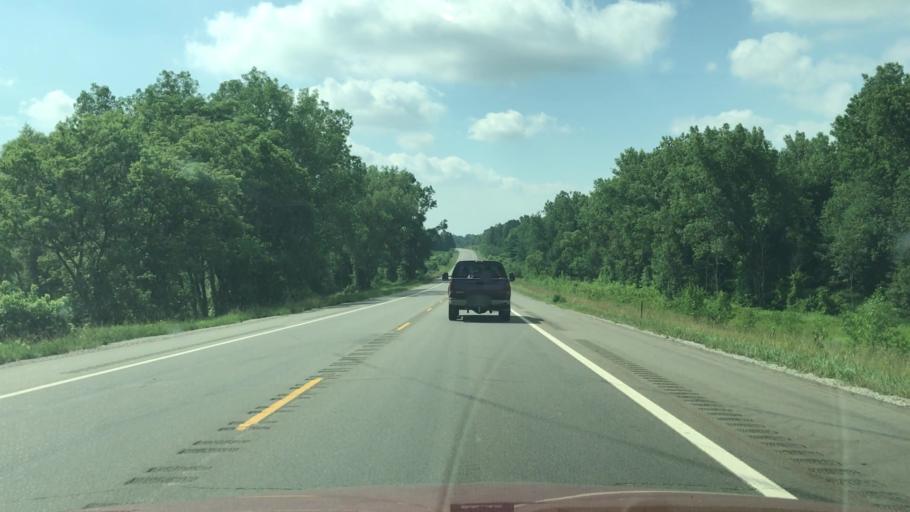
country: US
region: Michigan
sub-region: Kent County
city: Sparta
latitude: 43.1408
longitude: -85.7191
